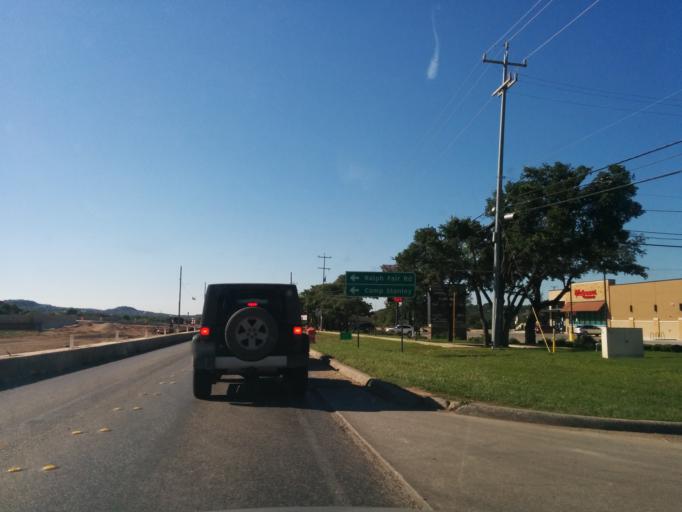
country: US
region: Texas
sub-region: Bexar County
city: Cross Mountain
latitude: 29.6769
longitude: -98.6374
